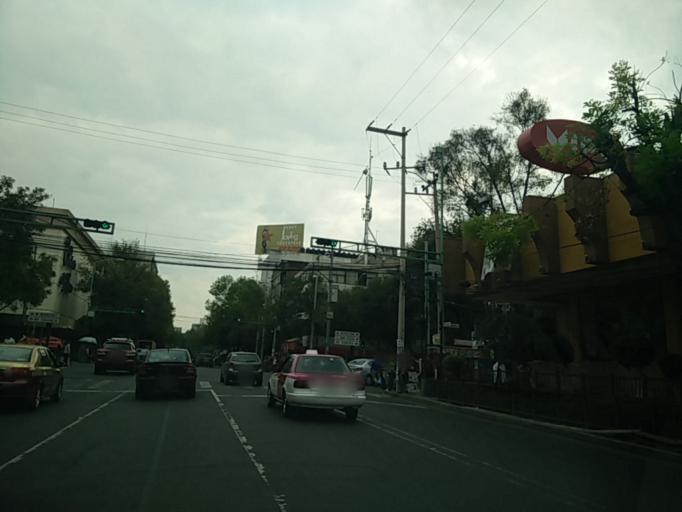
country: MX
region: Mexico City
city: Benito Juarez
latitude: 19.4197
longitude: -99.1697
